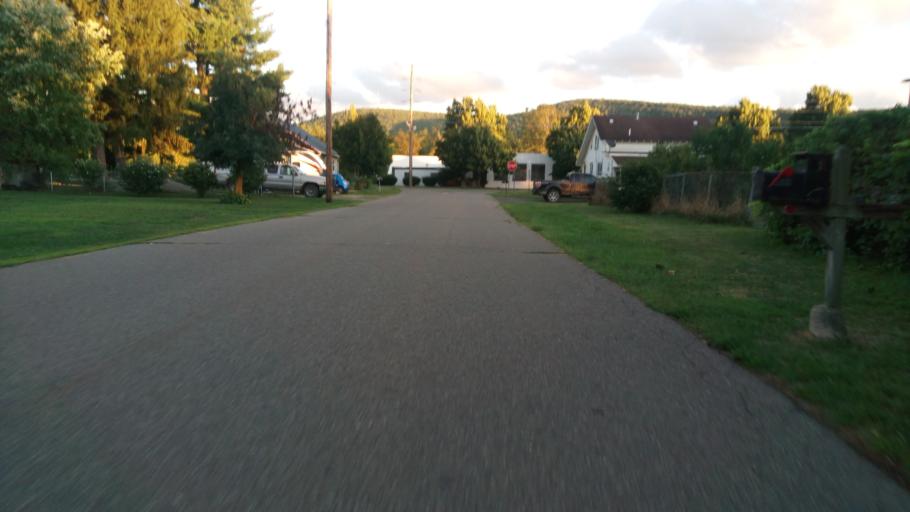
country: US
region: New York
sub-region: Chemung County
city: Southport
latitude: 42.0597
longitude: -76.7911
